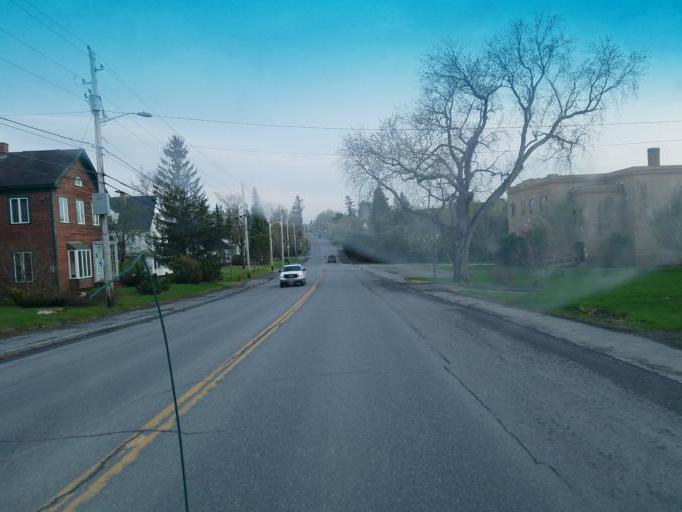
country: US
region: Maine
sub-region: Aroostook County
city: Caribou
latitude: 46.8562
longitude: -68.0110
